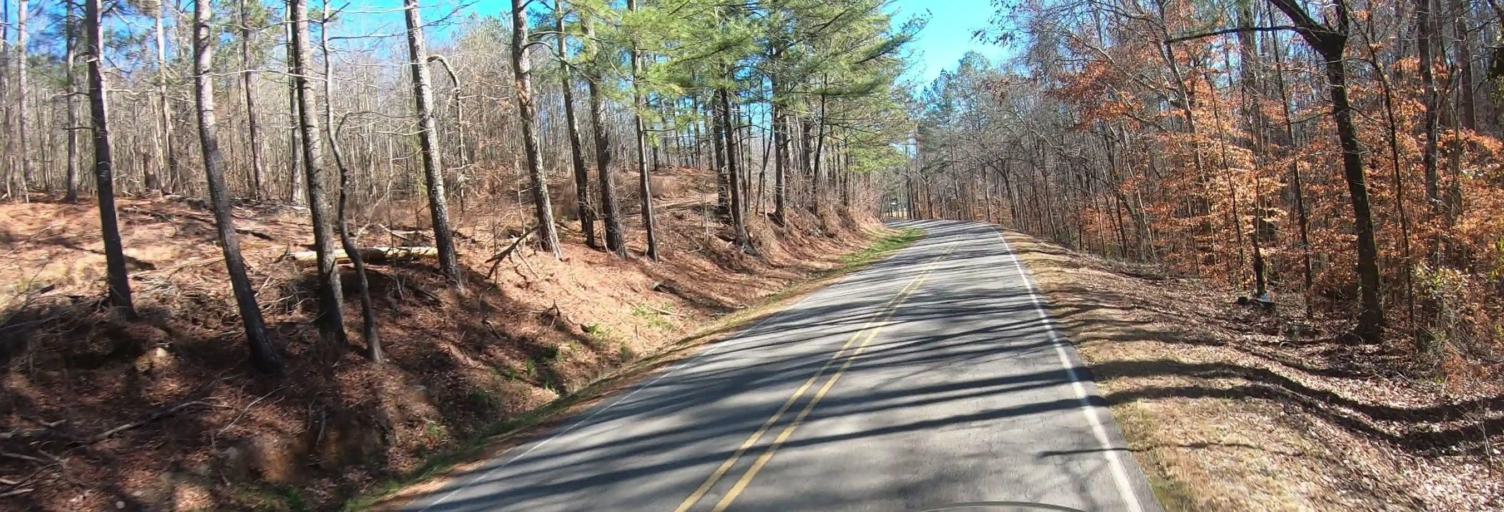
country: US
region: Alabama
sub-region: Clay County
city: Ashland
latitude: 33.3630
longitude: -85.9136
